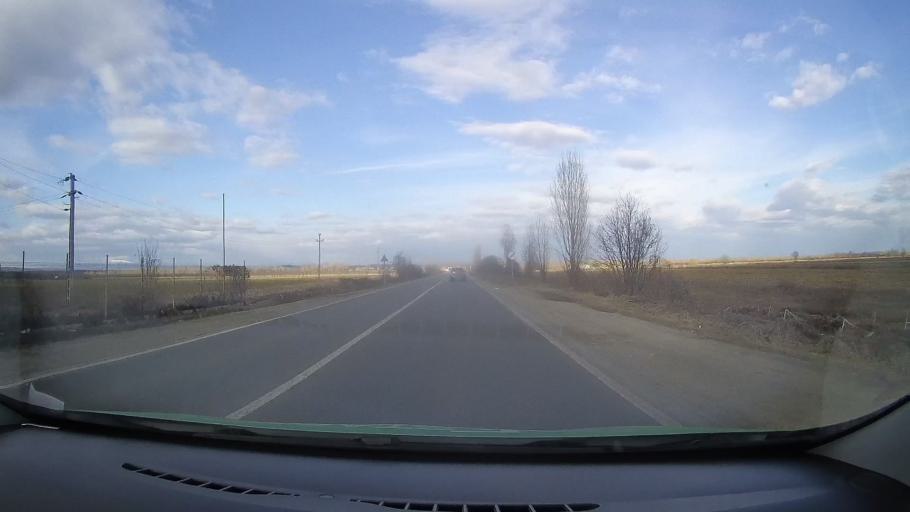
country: RO
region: Dambovita
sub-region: Comuna Ulmi
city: Ulmi
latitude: 44.8985
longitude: 25.4994
